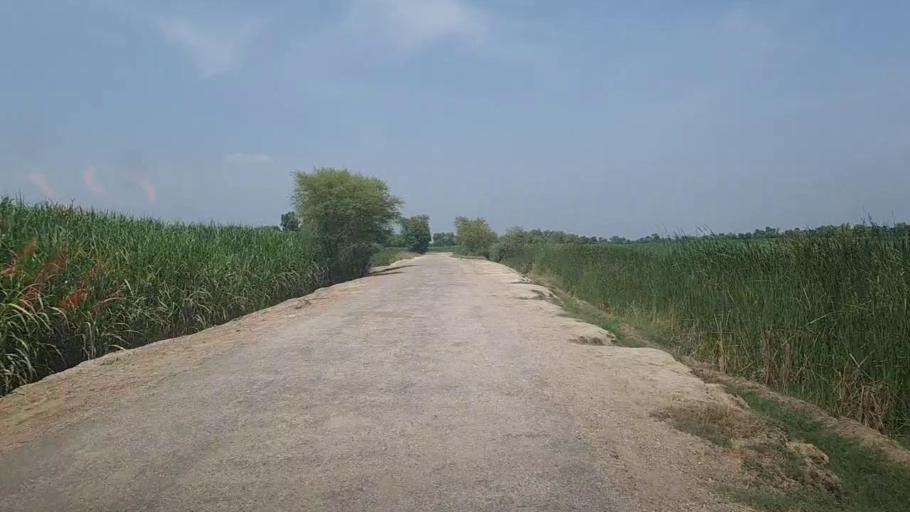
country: PK
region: Sindh
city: Ubauro
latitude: 28.1630
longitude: 69.8283
